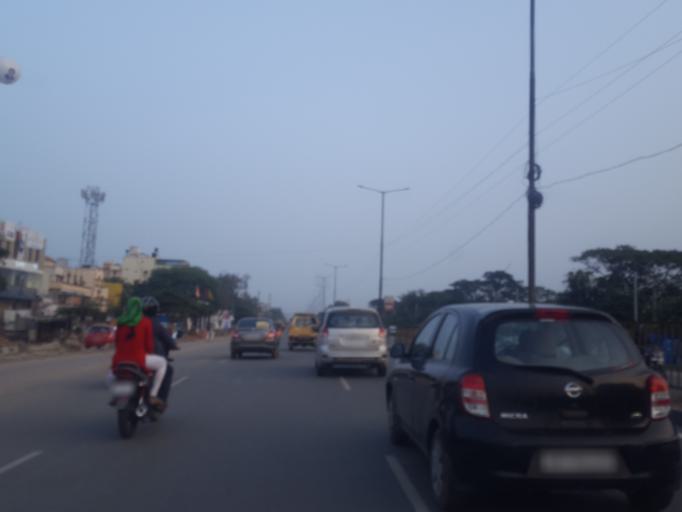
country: IN
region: Telangana
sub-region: Medak
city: Serilingampalle
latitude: 17.5068
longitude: 78.3044
